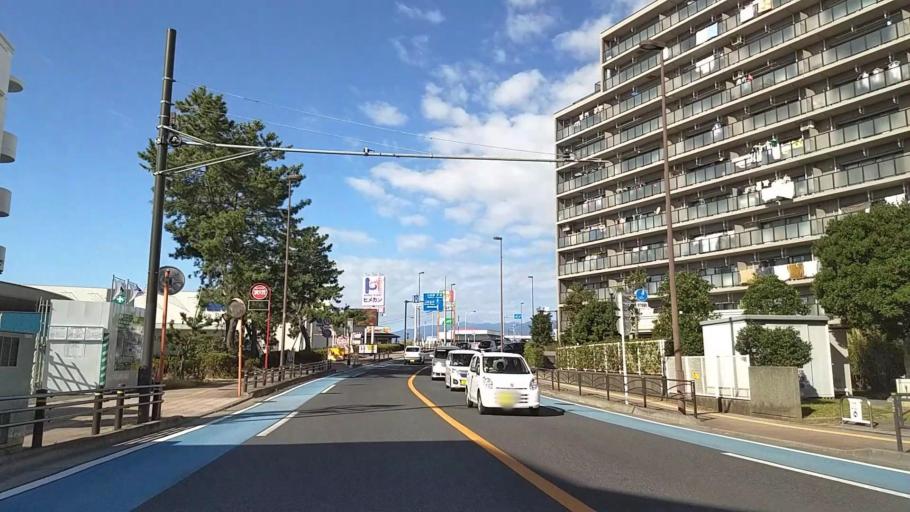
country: JP
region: Kanagawa
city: Chigasaki
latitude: 35.3289
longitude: 139.3911
